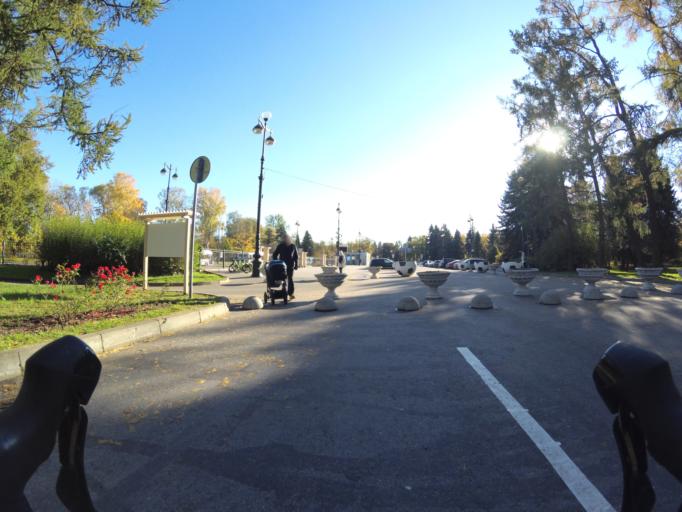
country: RU
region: Leningrad
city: Krestovskiy ostrov
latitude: 59.9697
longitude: 30.2464
